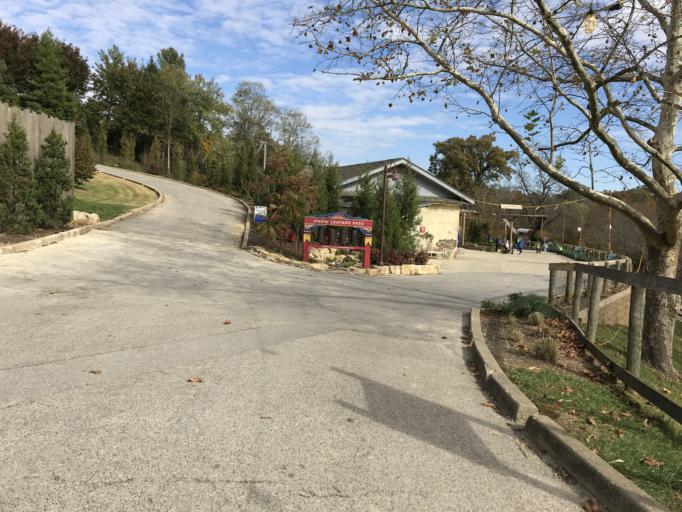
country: US
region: Kentucky
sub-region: Jefferson County
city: Audubon Park
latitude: 38.2053
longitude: -85.7023
